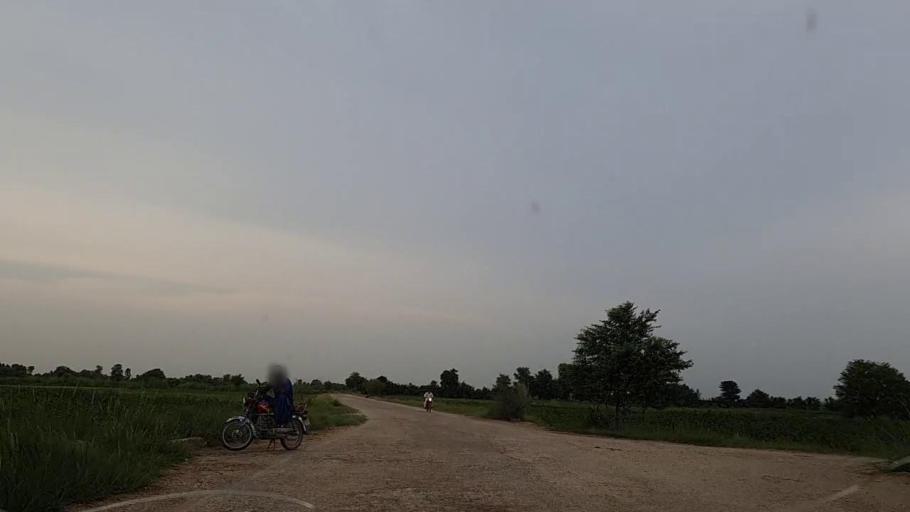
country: PK
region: Sindh
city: Mirpur Mathelo
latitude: 27.8756
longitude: 69.6364
